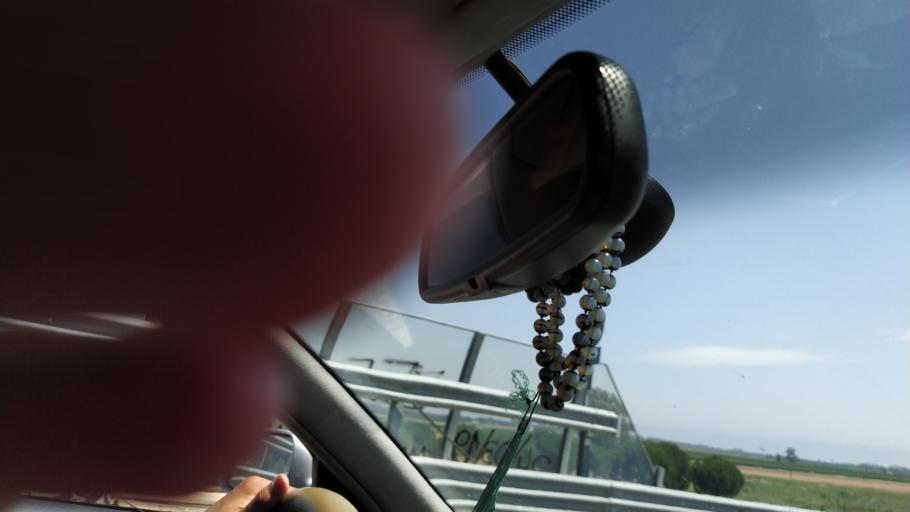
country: IT
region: Basilicate
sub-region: Provincia di Matera
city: Marconia
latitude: 40.3409
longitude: 16.7612
